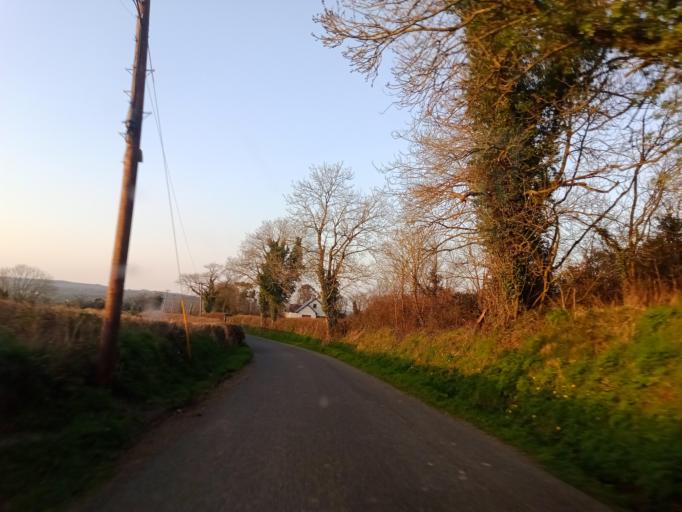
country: IE
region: Leinster
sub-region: Kilkenny
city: Castlecomer
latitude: 52.7383
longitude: -7.2372
